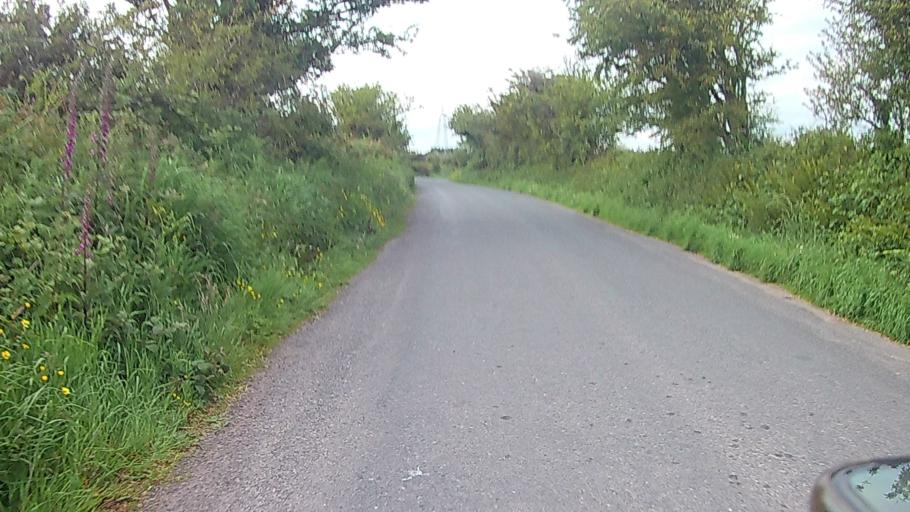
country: IE
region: Munster
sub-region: County Cork
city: Watergrasshill
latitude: 51.9712
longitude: -8.4118
